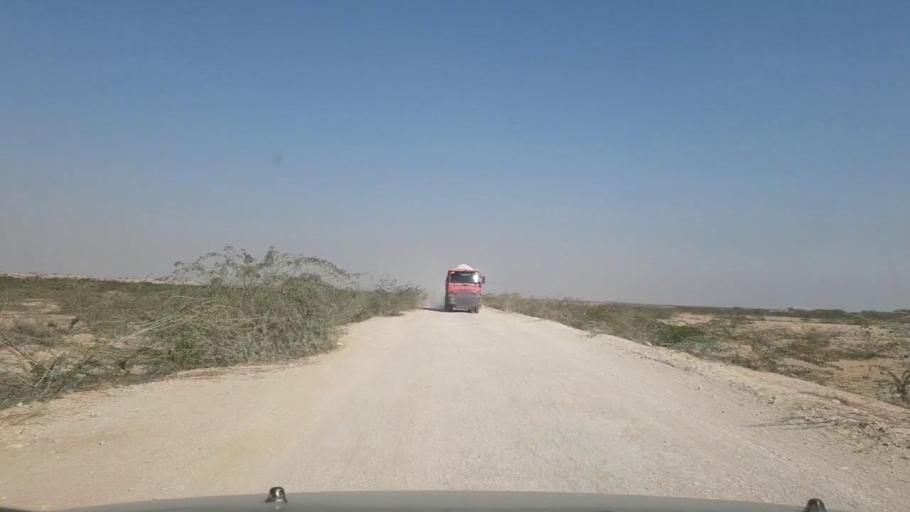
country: PK
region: Sindh
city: Thatta
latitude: 24.9644
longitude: 67.9628
